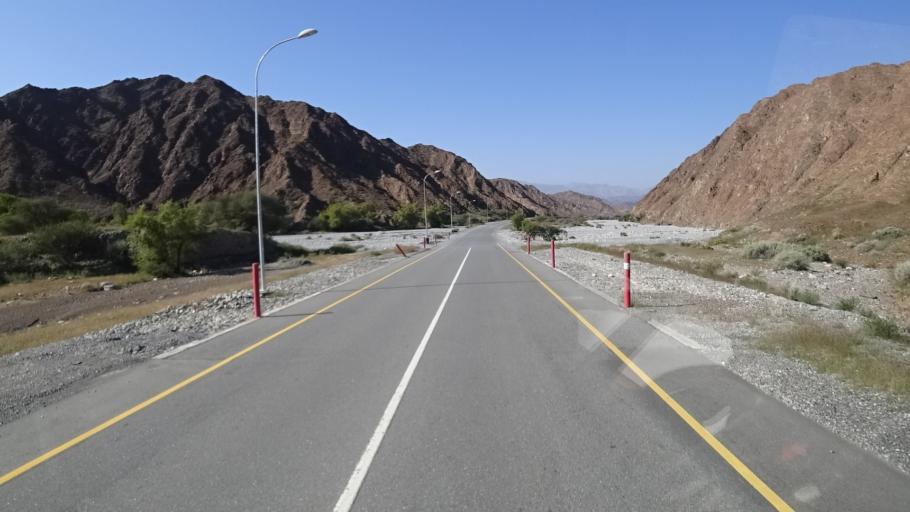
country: OM
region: Al Batinah
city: Bayt al `Awabi
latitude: 23.3615
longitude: 57.6665
